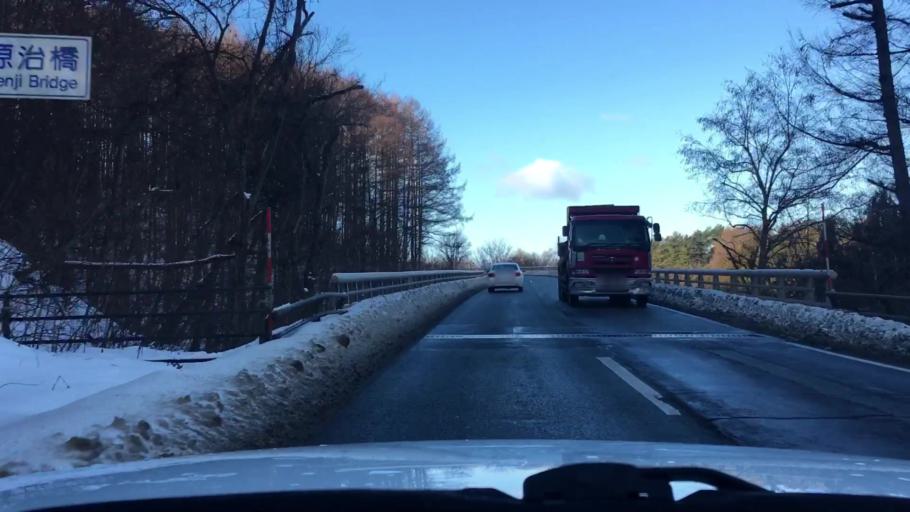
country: JP
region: Iwate
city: Morioka-shi
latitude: 39.6648
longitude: 141.3293
